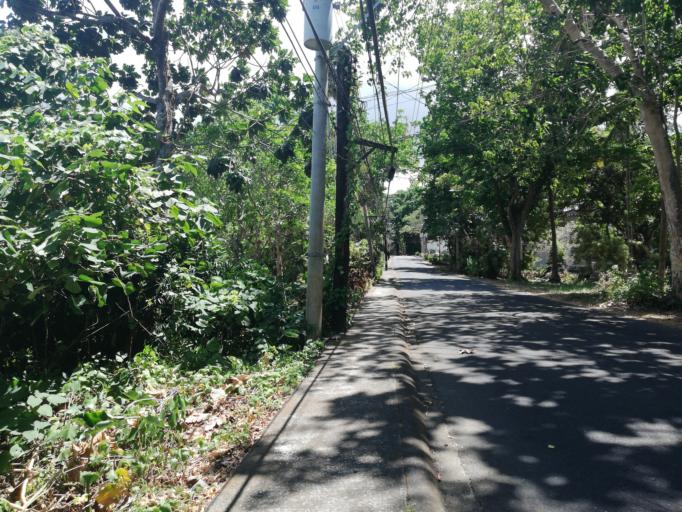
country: PH
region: Calabarzon
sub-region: Province of Laguna
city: Los Banos
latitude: 14.1613
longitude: 121.2383
